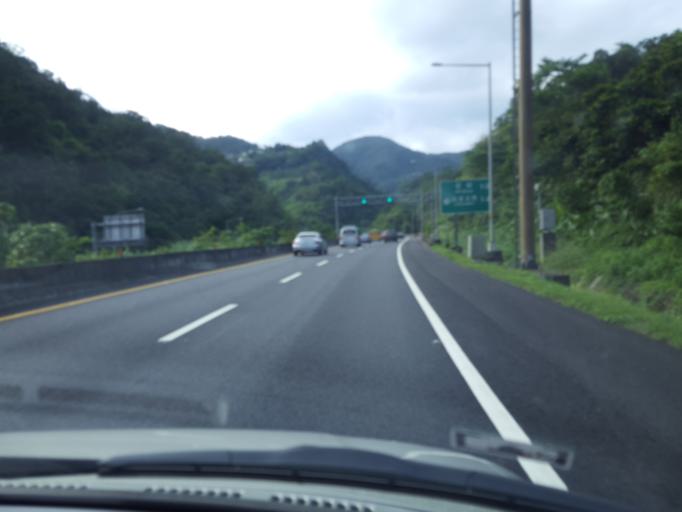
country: TW
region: Taiwan
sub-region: Keelung
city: Keelung
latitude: 24.9473
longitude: 121.7058
